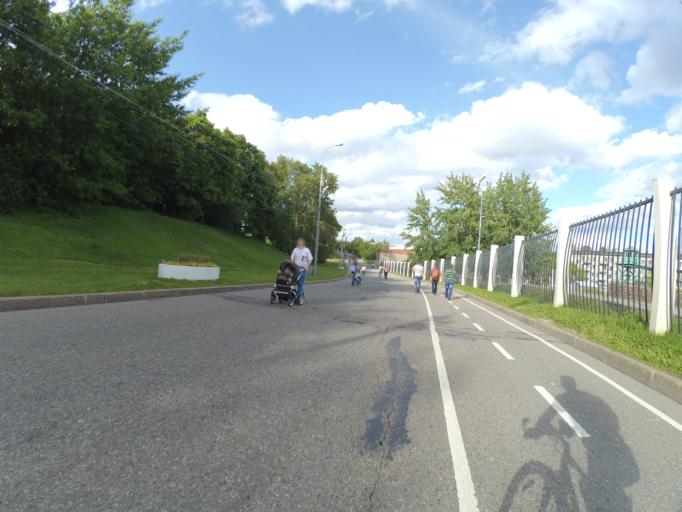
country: RU
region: Moskovskaya
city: Kastanayevo
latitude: 55.7287
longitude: 37.5070
